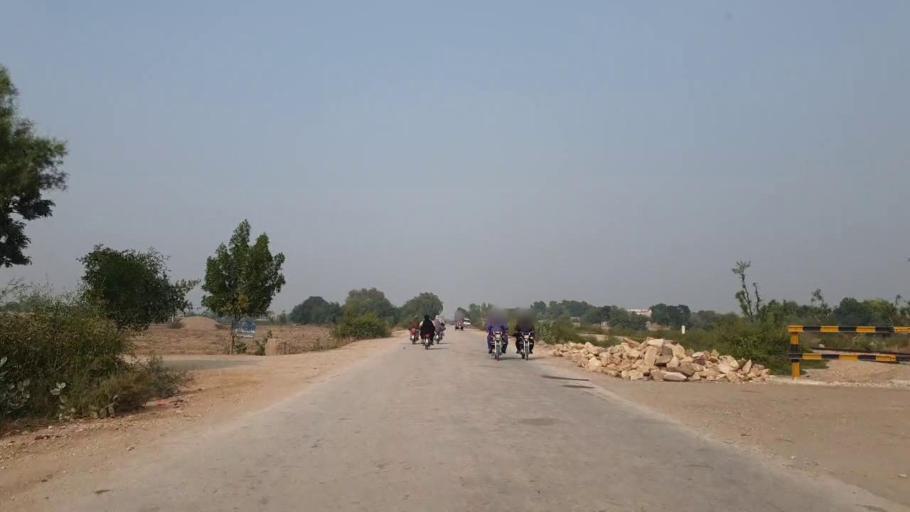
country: PK
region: Sindh
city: Bhan
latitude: 26.5743
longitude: 67.7275
